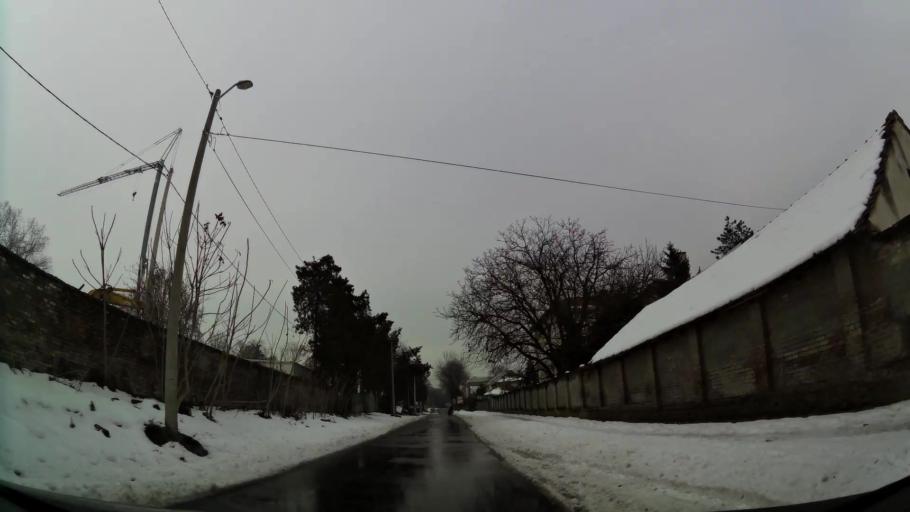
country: RS
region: Central Serbia
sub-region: Belgrade
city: Zemun
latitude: 44.8541
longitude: 20.3834
